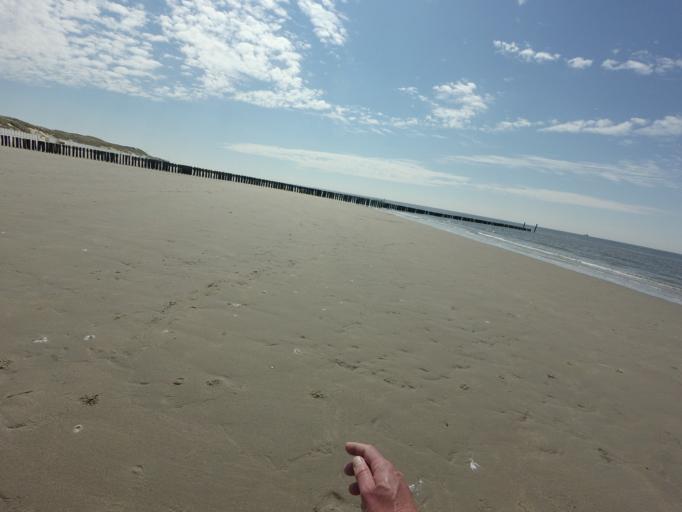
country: NL
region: Zeeland
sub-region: Gemeente Vlissingen
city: Vlissingen
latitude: 51.5166
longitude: 3.4478
